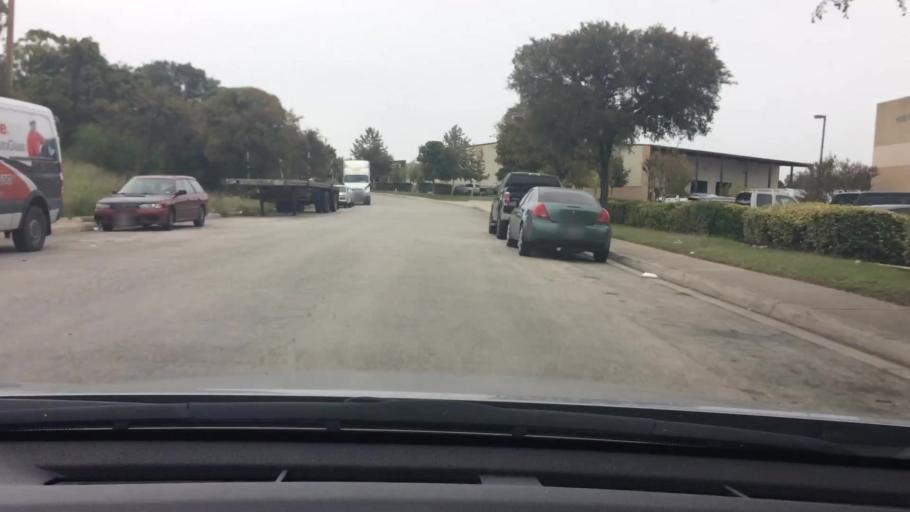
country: US
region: Texas
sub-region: Bexar County
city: Windcrest
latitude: 29.5409
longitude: -98.3722
